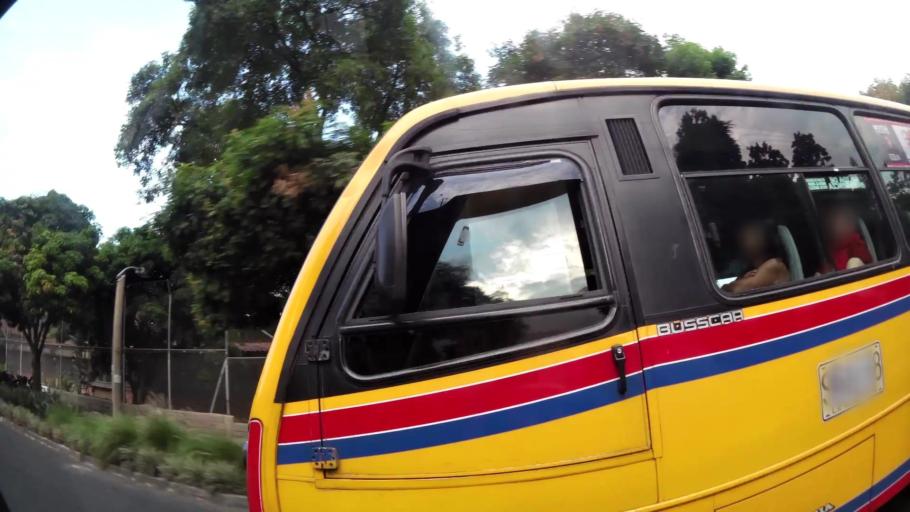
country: CO
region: Antioquia
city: Itagui
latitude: 6.2115
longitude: -75.5765
